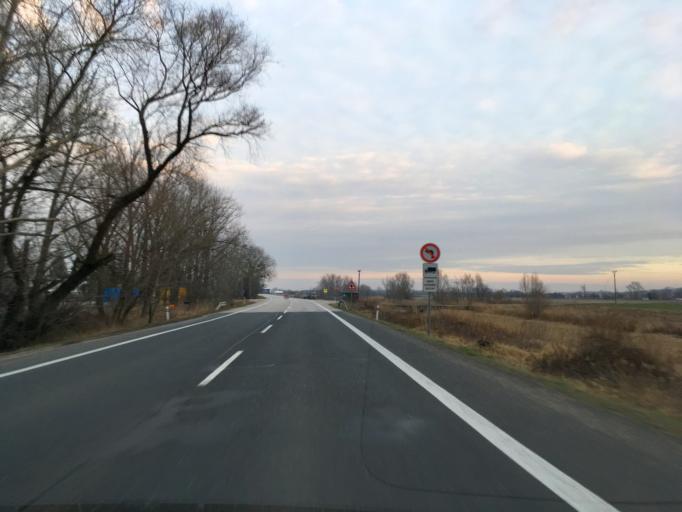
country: HU
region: Komarom-Esztergom
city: Acs
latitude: 47.7674
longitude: 17.9671
